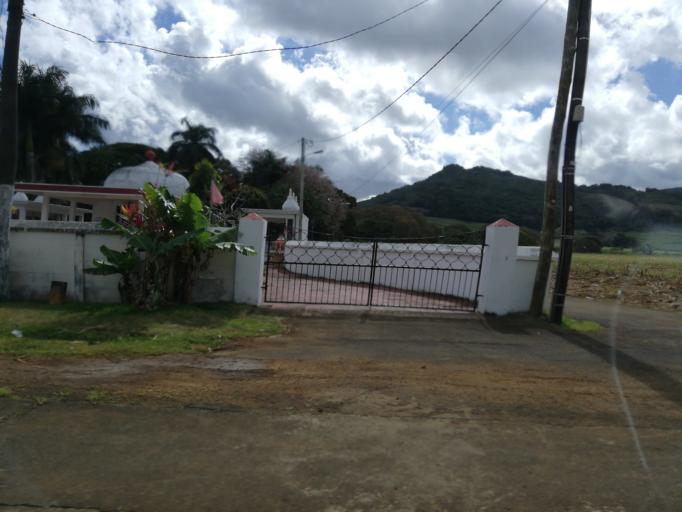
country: MU
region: Grand Port
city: Bois des Amourettes
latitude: -20.3677
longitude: 57.7028
